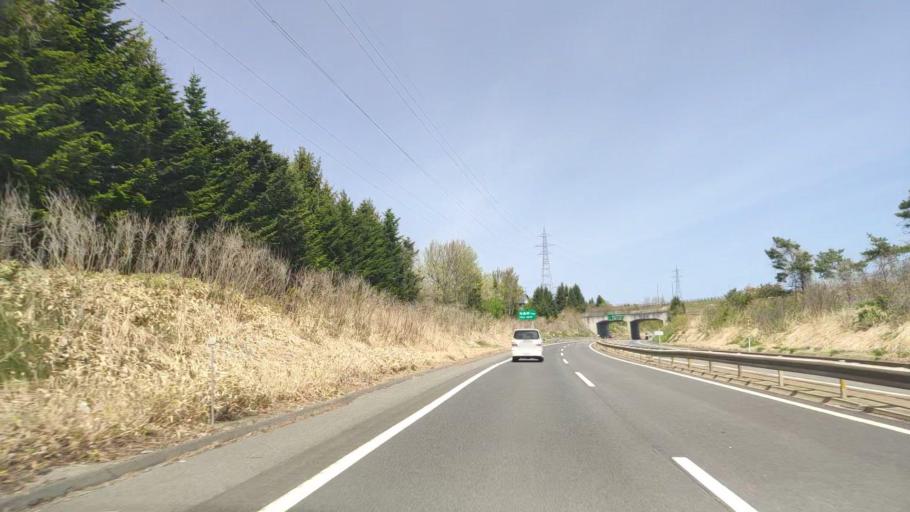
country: JP
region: Aomori
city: Hachinohe
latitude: 40.4762
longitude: 141.4598
